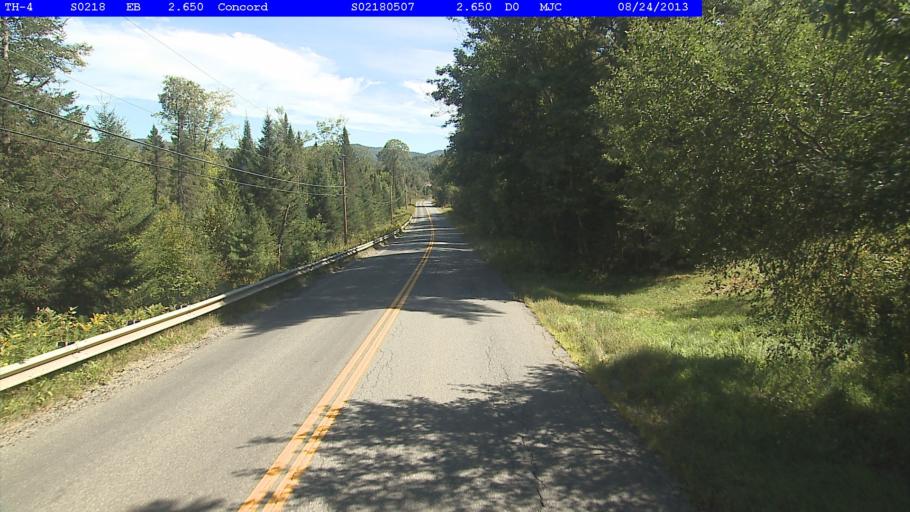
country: US
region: New Hampshire
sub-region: Grafton County
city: Littleton
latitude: 44.4306
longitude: -71.7535
